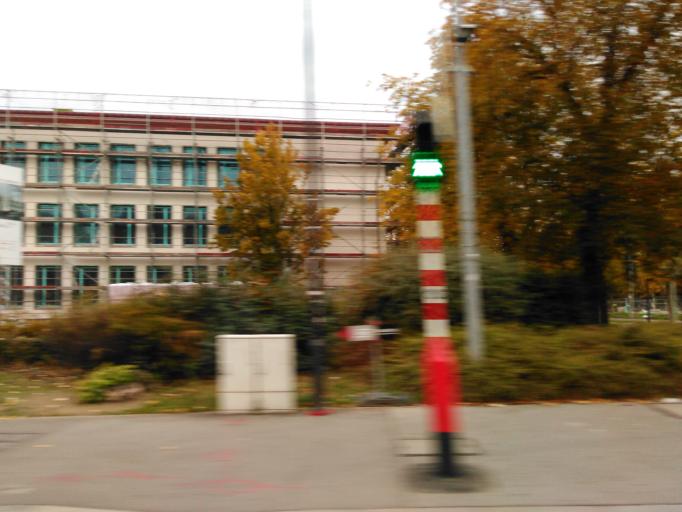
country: LU
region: Luxembourg
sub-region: Canton de Luxembourg
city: Luxembourg
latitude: 49.6151
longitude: 6.1216
